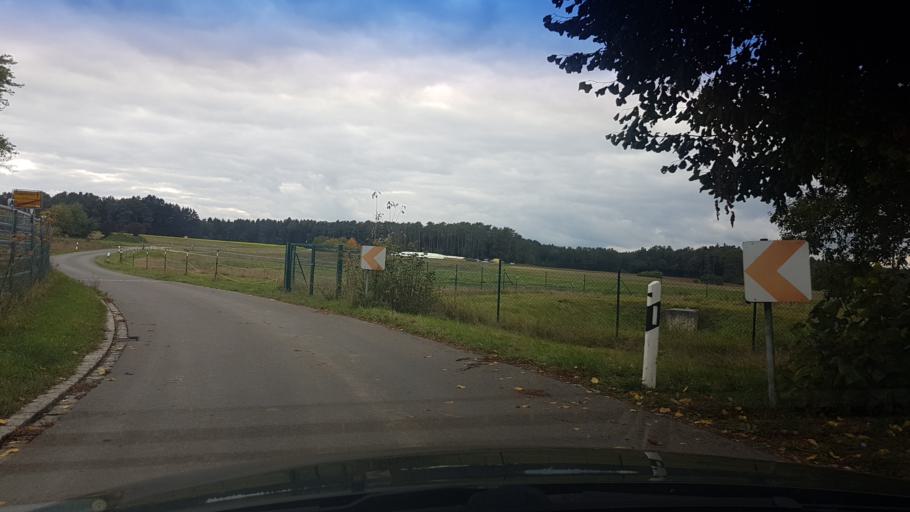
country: DE
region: Bavaria
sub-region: Upper Franconia
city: Stadelhofen
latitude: 50.0070
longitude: 11.2373
